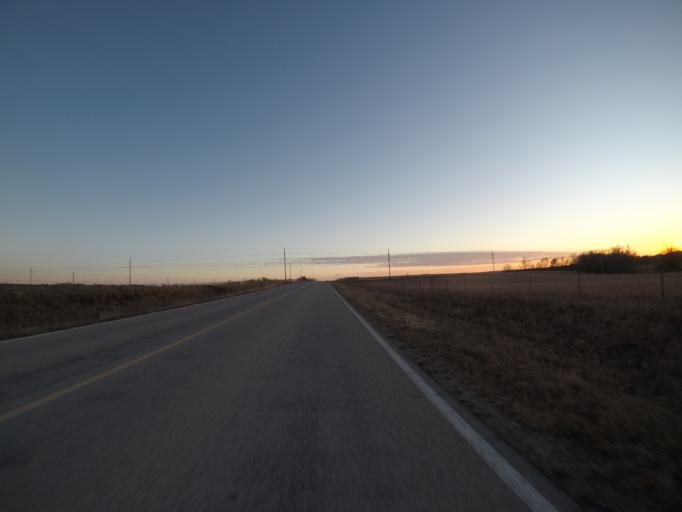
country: US
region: Kansas
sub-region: Riley County
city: Manhattan
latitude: 39.2269
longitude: -96.4825
